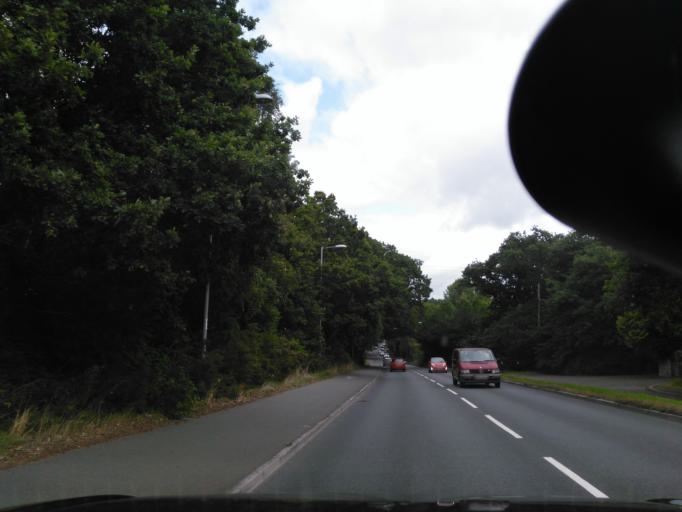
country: GB
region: England
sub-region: Dorset
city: Wareham
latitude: 50.6990
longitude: -2.1094
